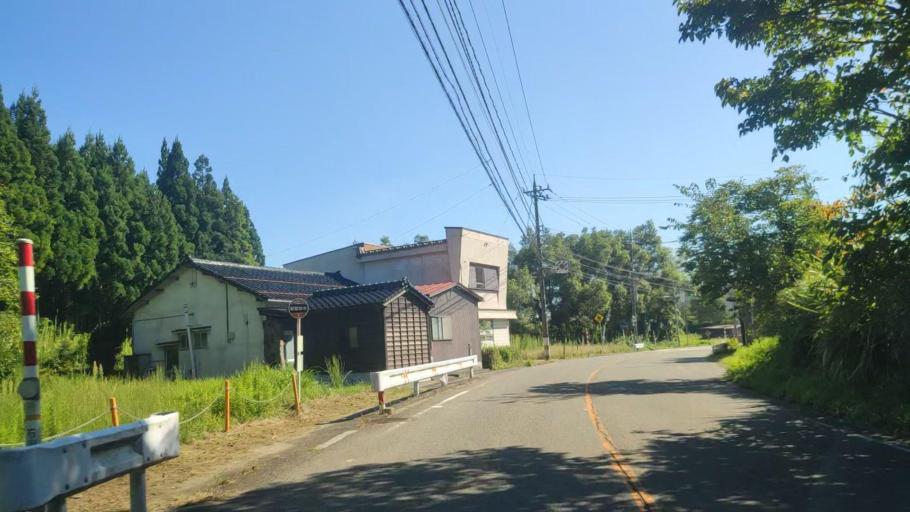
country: JP
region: Ishikawa
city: Nanao
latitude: 37.2578
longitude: 137.0894
